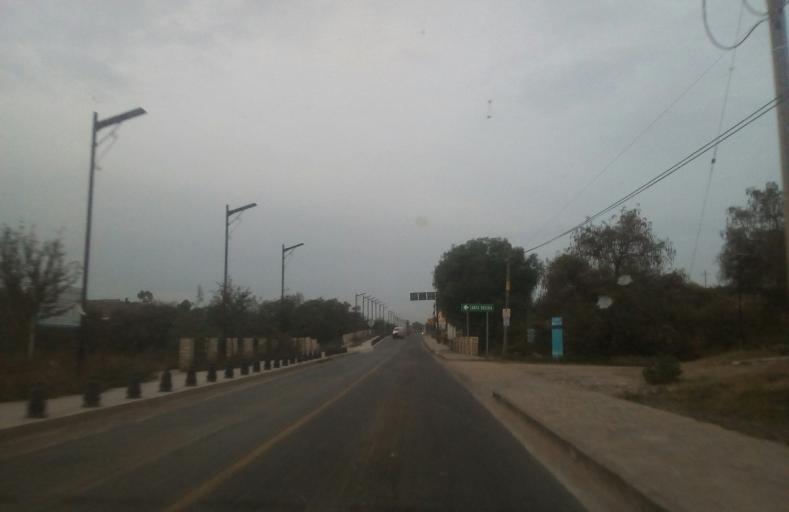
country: MX
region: Guanajuato
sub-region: San Luis de la Paz
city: San Ignacio
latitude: 21.2298
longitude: -100.4910
